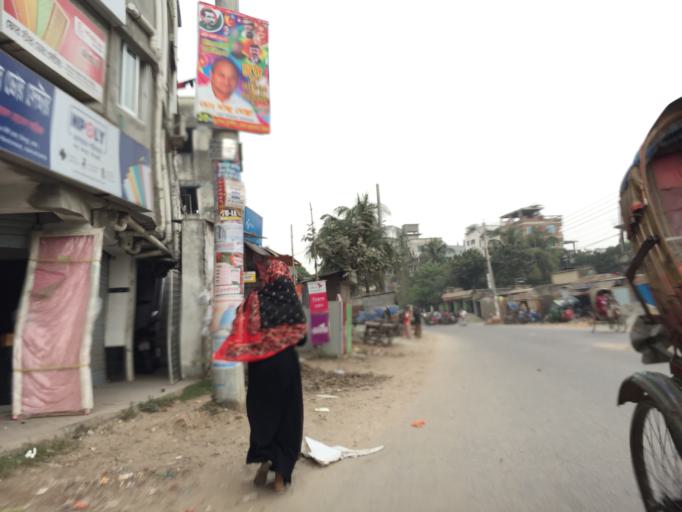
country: BD
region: Dhaka
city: Azimpur
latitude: 23.7941
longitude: 90.3653
